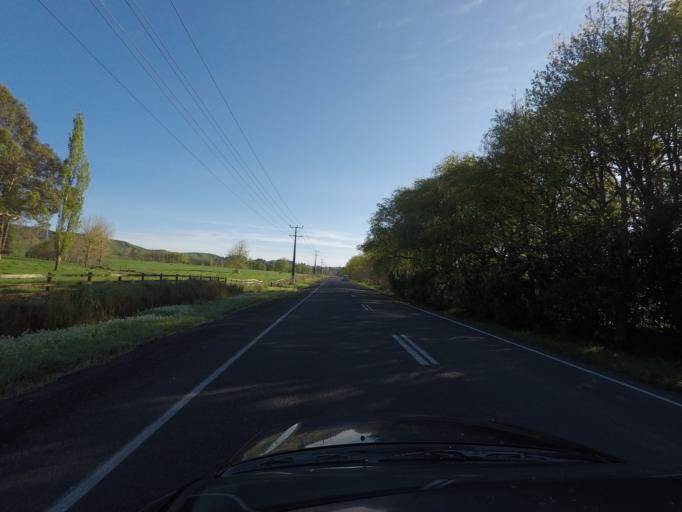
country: NZ
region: Auckland
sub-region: Auckland
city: Red Hill
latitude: -37.0094
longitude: 174.9524
